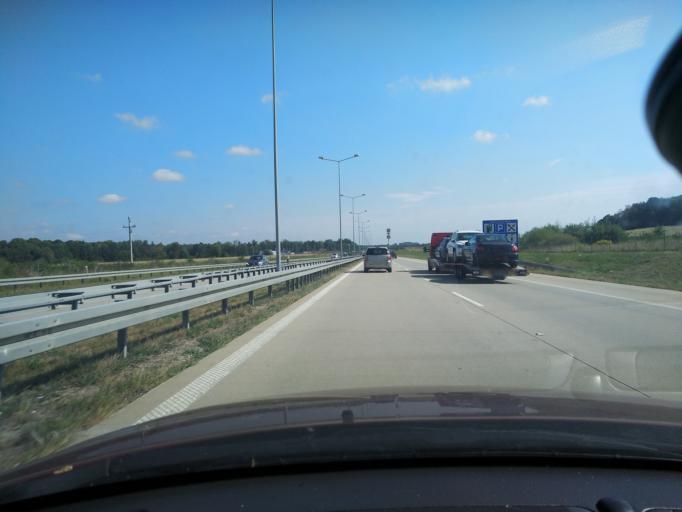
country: PL
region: Lower Silesian Voivodeship
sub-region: Powiat zgorzelecki
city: Lagow
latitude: 51.1846
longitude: 15.0998
